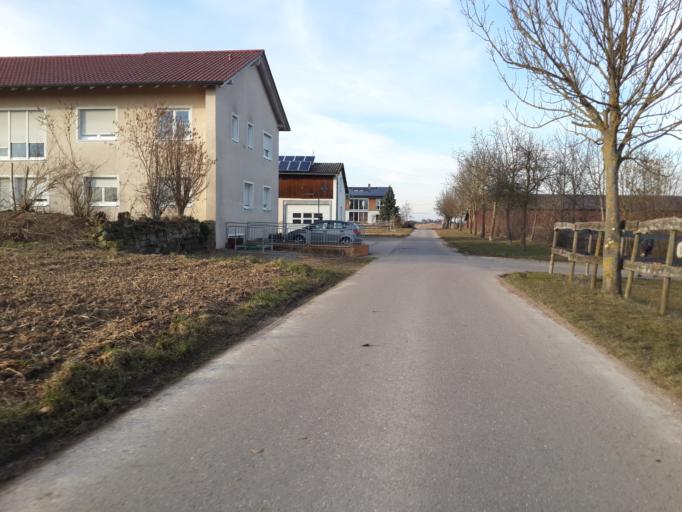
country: DE
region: Baden-Wuerttemberg
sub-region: Regierungsbezirk Stuttgart
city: Nordheim
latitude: 49.1181
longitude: 9.1229
